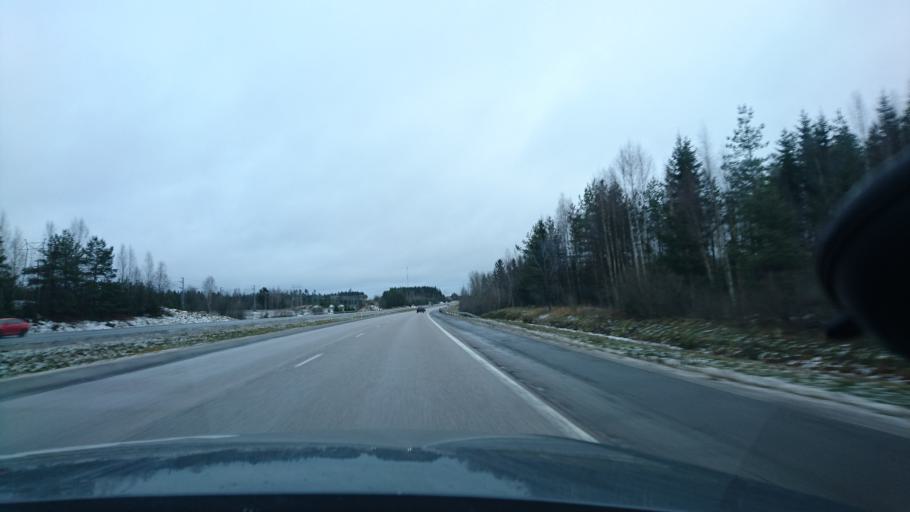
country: FI
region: Uusimaa
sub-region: Helsinki
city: Maentsaelae
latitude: 60.5882
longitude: 25.2295
